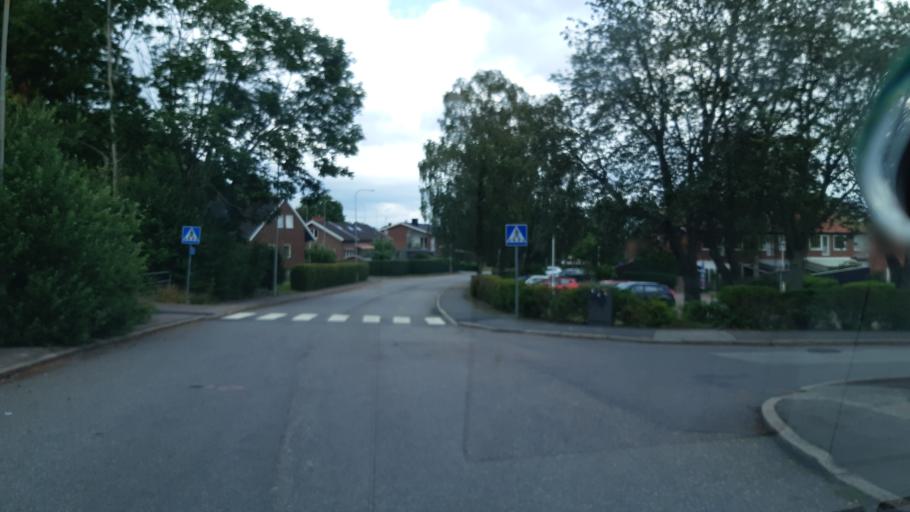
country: SE
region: Vaestra Goetaland
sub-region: Partille Kommun
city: Partille
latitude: 57.7162
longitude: 12.0605
